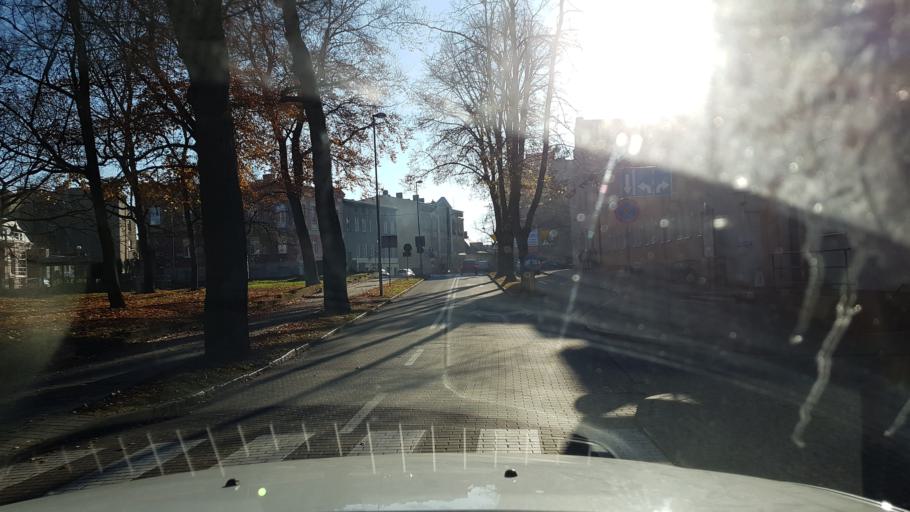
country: PL
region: West Pomeranian Voivodeship
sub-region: Powiat stargardzki
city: Stargard Szczecinski
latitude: 53.3350
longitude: 15.0386
